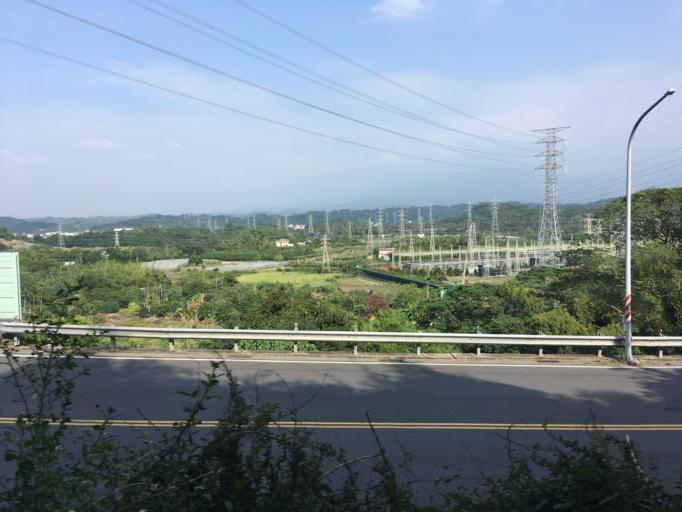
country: TW
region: Taiwan
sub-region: Chiayi
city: Jiayi Shi
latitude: 23.4954
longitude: 120.4843
